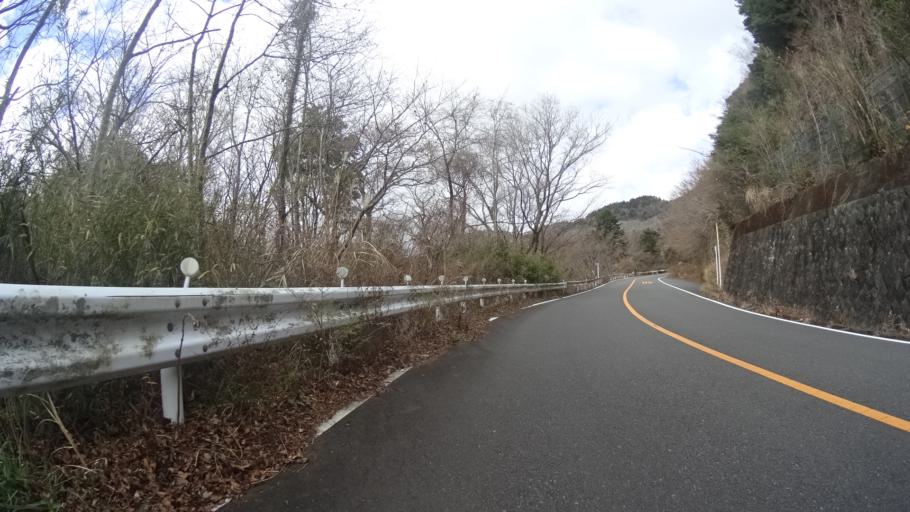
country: JP
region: Kanagawa
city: Yugawara
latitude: 35.1756
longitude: 139.0643
